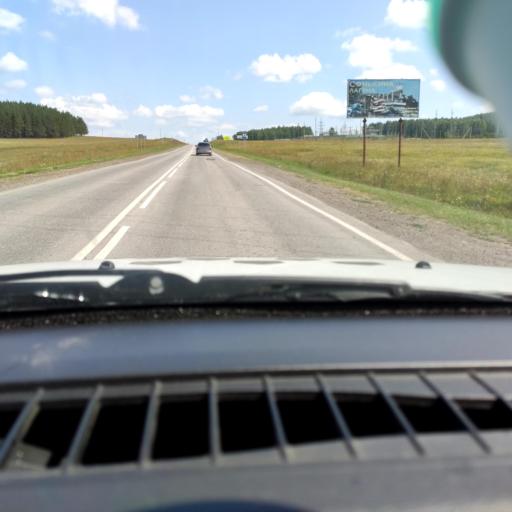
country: RU
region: Bashkortostan
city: Verkhniye Kigi
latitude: 55.3979
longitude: 58.6149
